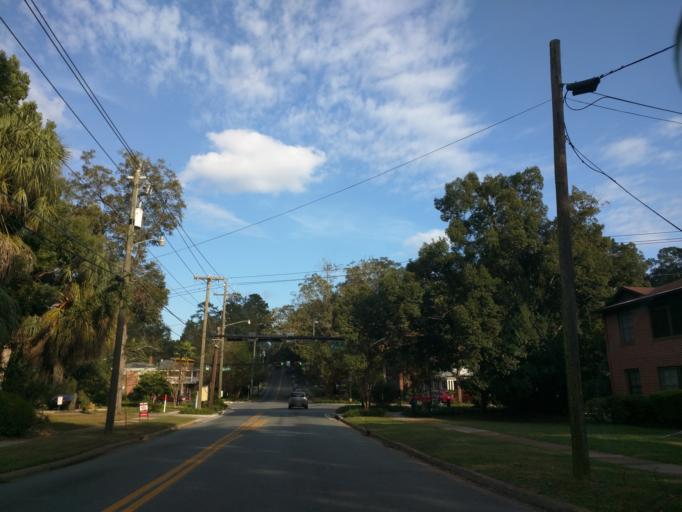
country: US
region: Florida
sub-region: Leon County
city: Tallahassee
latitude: 30.4418
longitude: -84.2755
